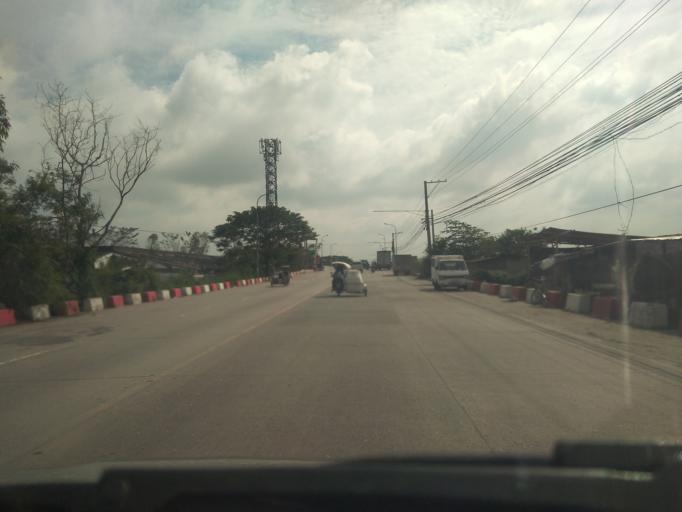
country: PH
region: Central Luzon
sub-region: Province of Pampanga
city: Pau
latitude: 15.0054
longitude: 120.7174
